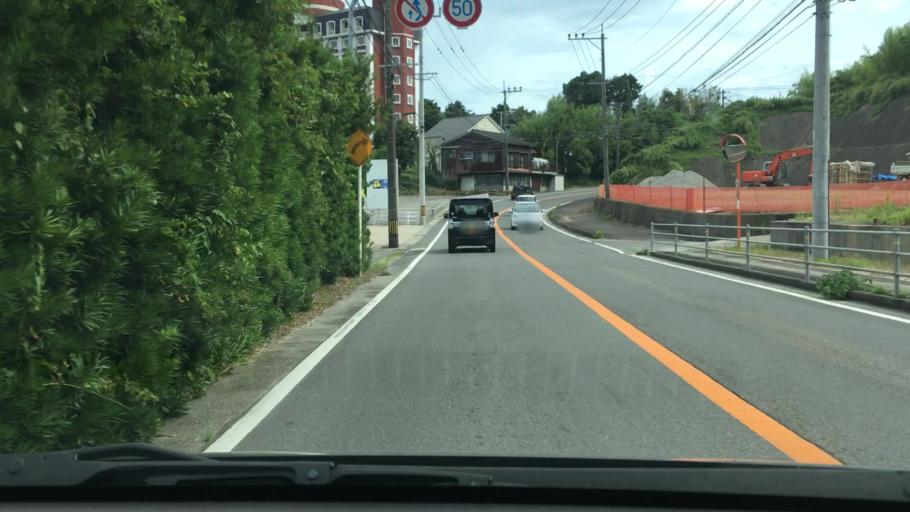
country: JP
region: Nagasaki
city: Togitsu
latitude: 32.8793
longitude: 129.7898
